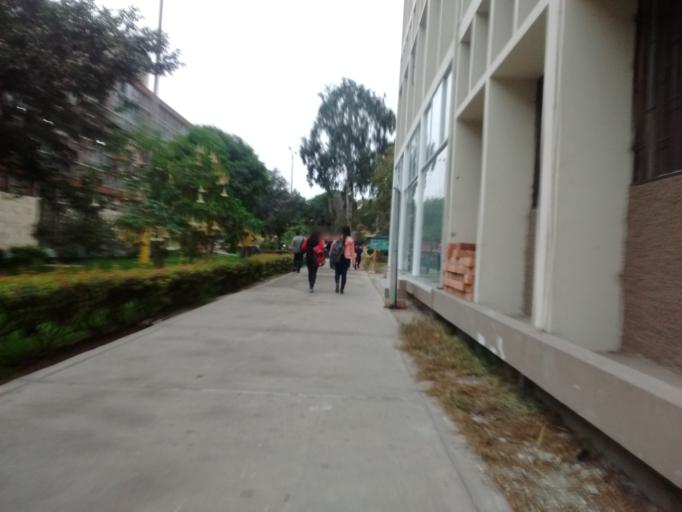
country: PE
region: Callao
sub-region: Callao
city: Callao
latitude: -12.0601
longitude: -77.0814
